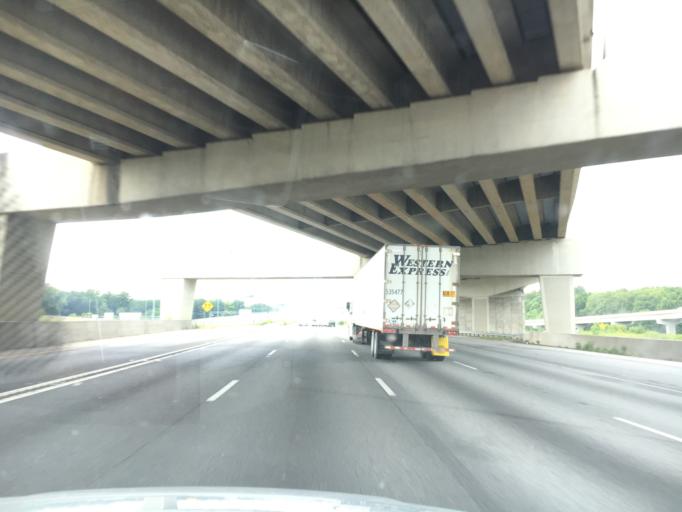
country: US
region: Georgia
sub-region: Gwinnett County
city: Duluth
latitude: 33.9653
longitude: -84.1006
